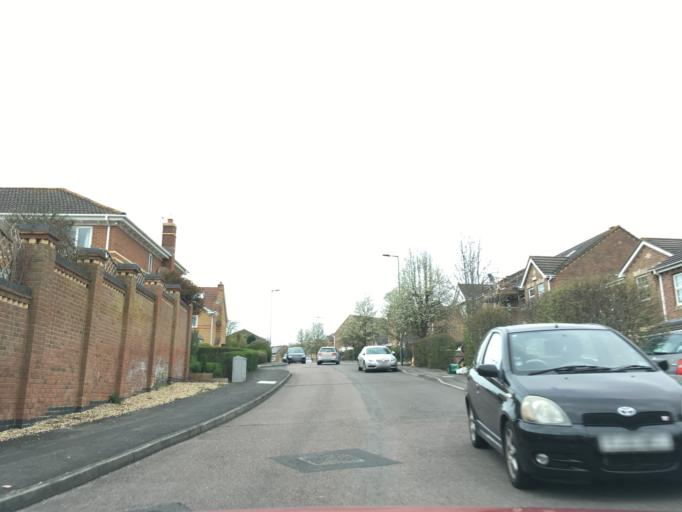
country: GB
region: England
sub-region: South Gloucestershire
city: Stoke Gifford
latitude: 51.5299
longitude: -2.5465
